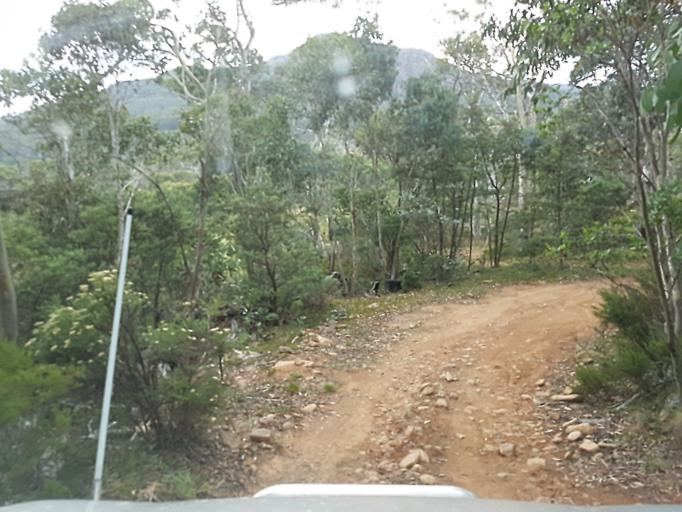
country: AU
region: New South Wales
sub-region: Snowy River
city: Jindabyne
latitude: -36.8808
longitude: 148.1596
